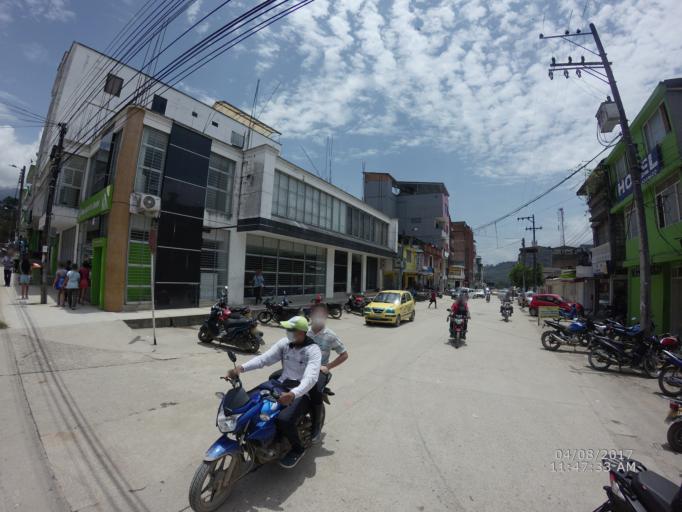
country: CO
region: Putumayo
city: Mocoa
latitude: 1.1458
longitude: -76.6475
